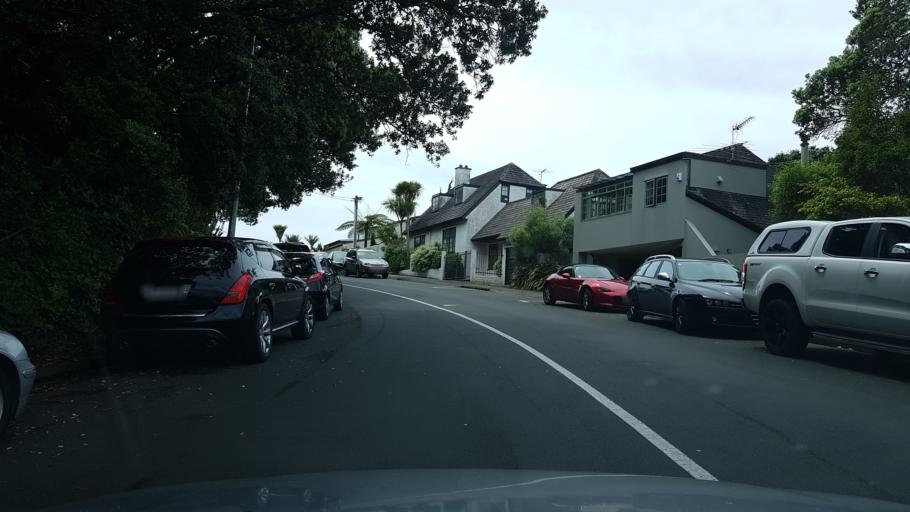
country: NZ
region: Auckland
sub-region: Auckland
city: North Shore
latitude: -36.8213
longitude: 174.7366
